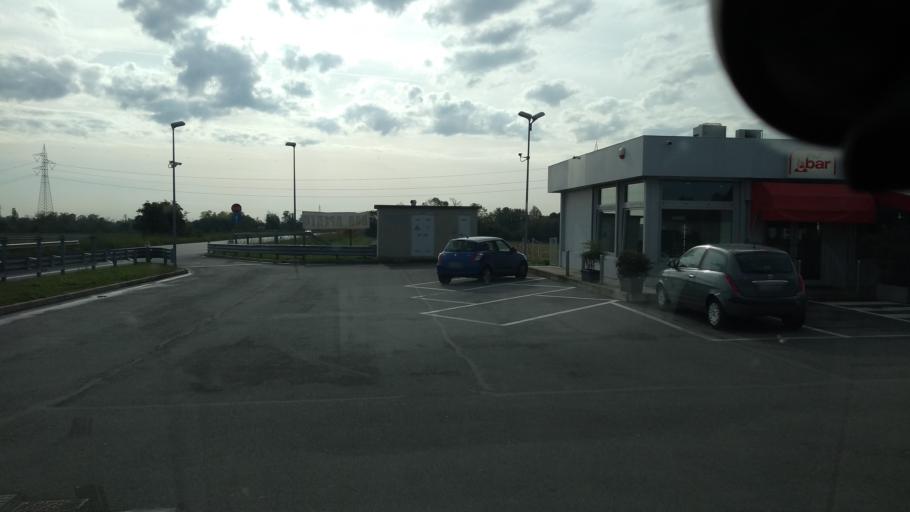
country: IT
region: Lombardy
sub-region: Provincia di Bergamo
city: Grassobbio
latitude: 45.6453
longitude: 9.7078
